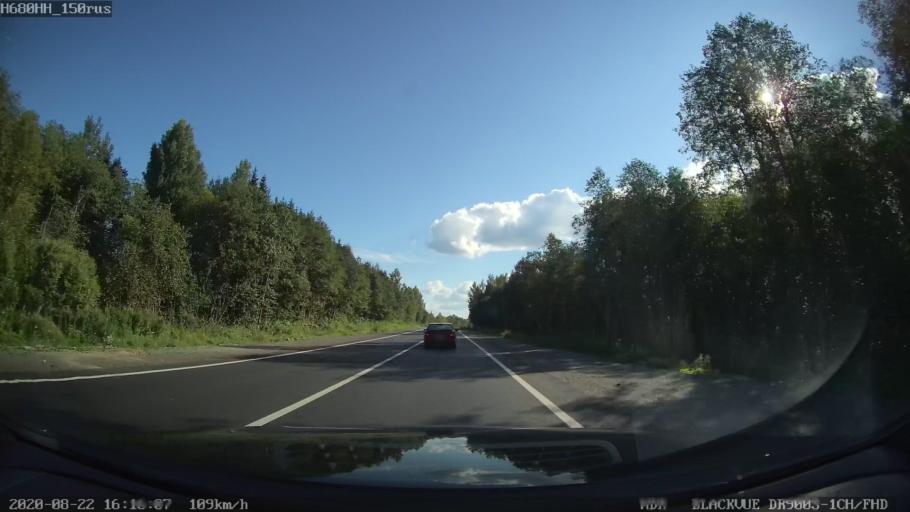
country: RU
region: Tverskaya
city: Rameshki
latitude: 57.4385
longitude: 36.1832
